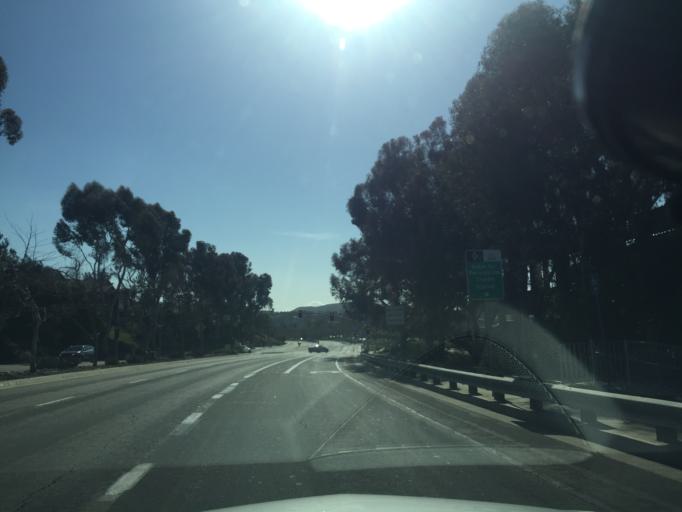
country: US
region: California
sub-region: San Diego County
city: Poway
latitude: 32.9637
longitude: -117.0908
